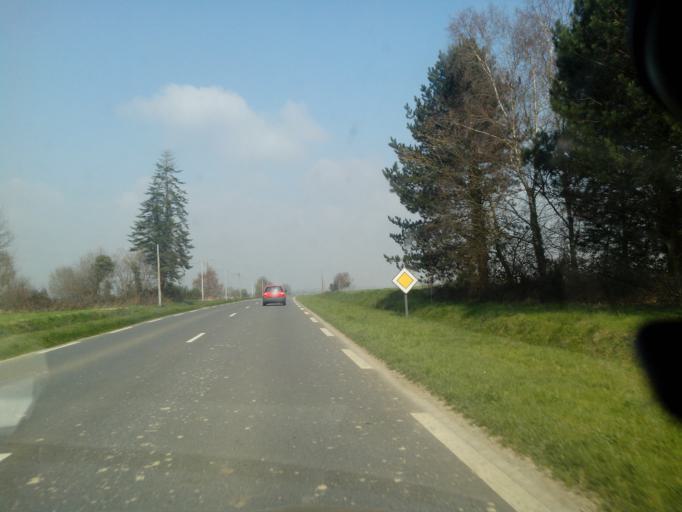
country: FR
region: Brittany
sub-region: Departement d'Ille-et-Vilaine
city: Quedillac
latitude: 48.2322
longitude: -2.1746
